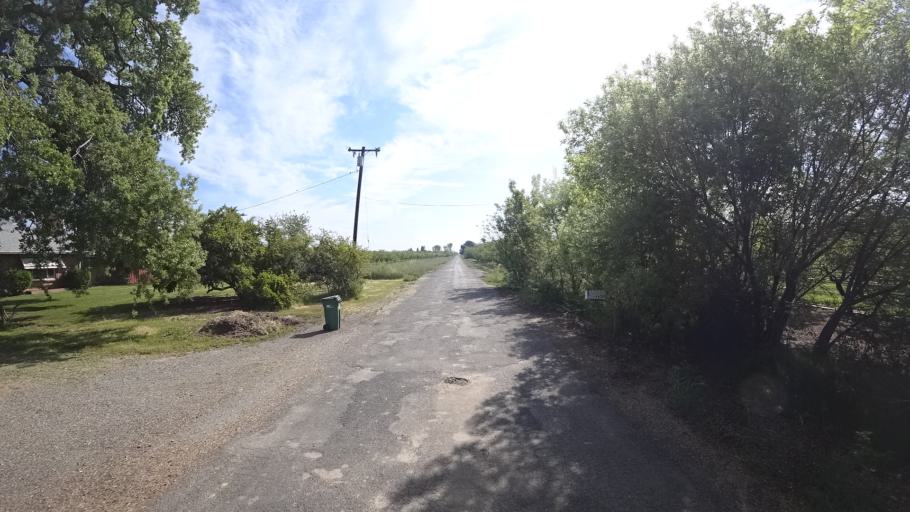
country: US
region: California
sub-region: Glenn County
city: Hamilton City
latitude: 39.6234
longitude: -122.0326
